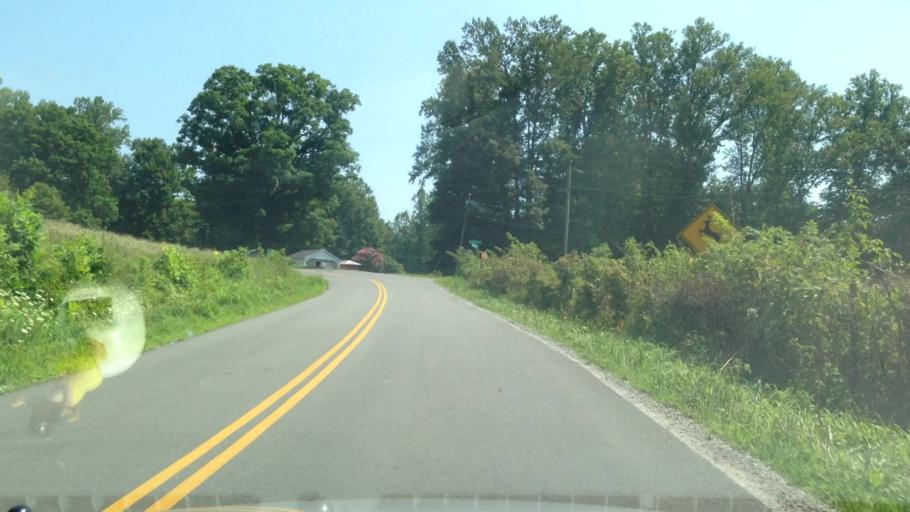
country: US
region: Virginia
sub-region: Patrick County
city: Patrick Springs
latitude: 36.5762
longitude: -80.1926
